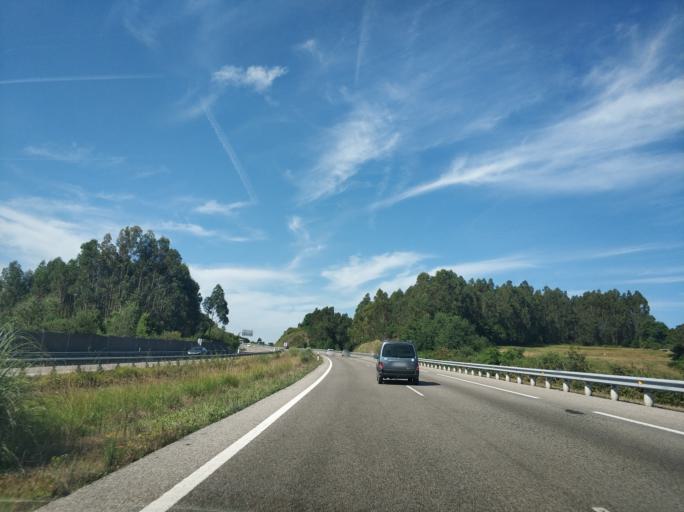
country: ES
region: Asturias
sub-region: Province of Asturias
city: Soto del Barco
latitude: 43.5236
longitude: -6.0573
